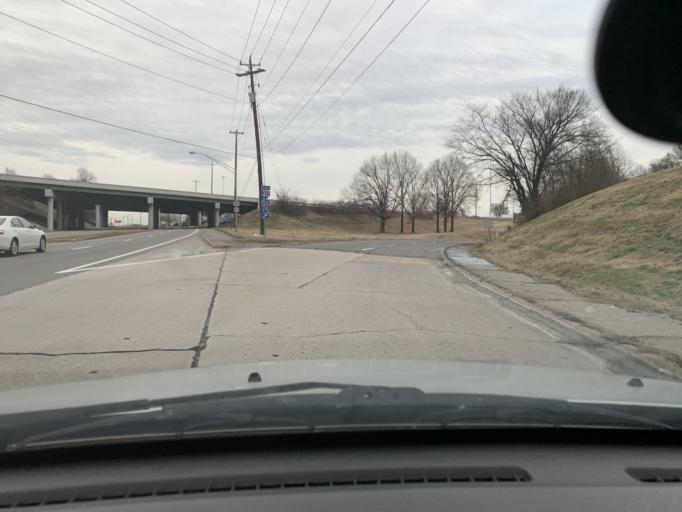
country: US
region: Tennessee
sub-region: Davidson County
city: Nashville
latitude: 36.1361
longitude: -86.7253
